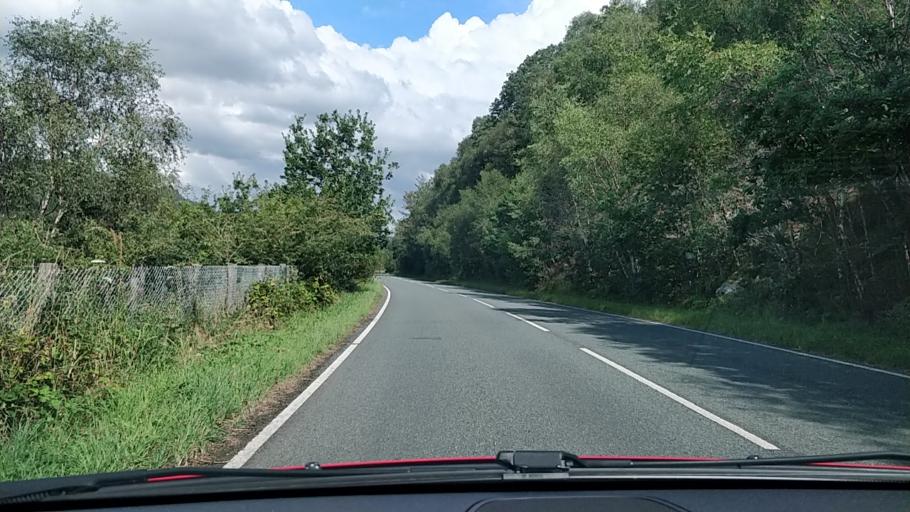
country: GB
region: Wales
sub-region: Gwynedd
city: Penrhyndeudraeth
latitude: 52.9352
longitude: -4.0338
